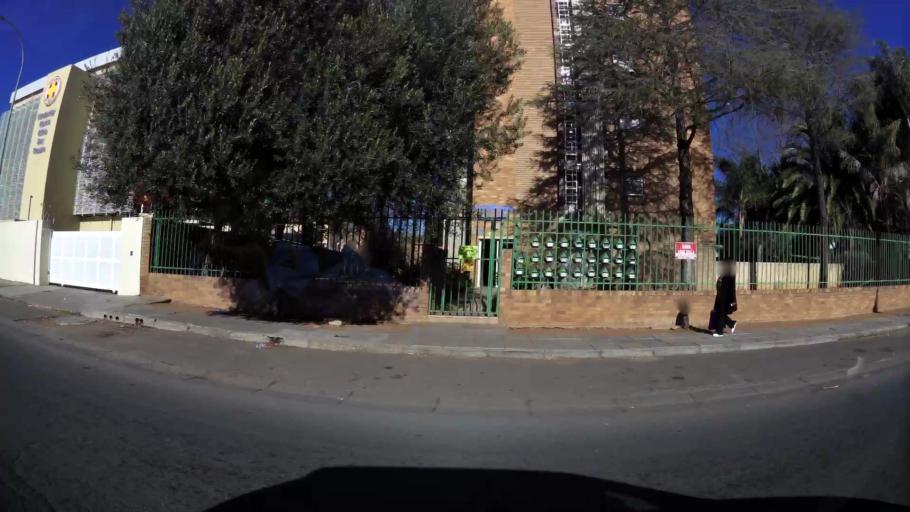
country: ZA
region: Northern Cape
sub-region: Frances Baard District Municipality
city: Kimberley
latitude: -28.7441
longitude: 24.7712
